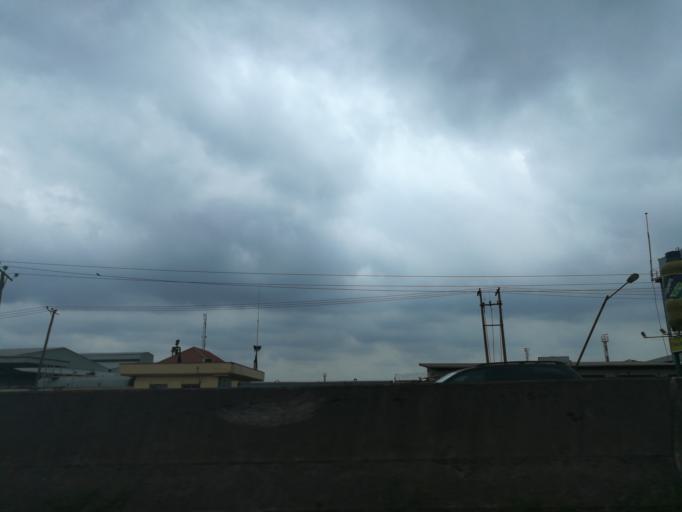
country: NG
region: Lagos
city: Somolu
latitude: 6.5478
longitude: 3.3829
